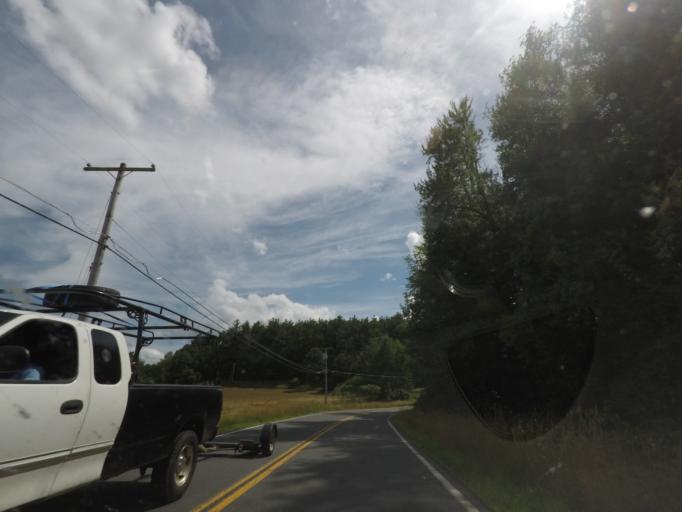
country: US
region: New York
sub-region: Rensselaer County
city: Wynantskill
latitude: 42.7054
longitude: -73.6115
